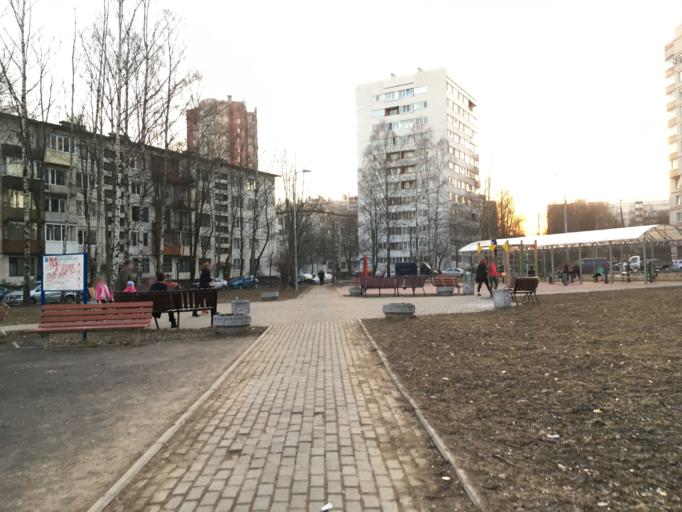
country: RU
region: St.-Petersburg
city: Grazhdanka
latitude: 60.0295
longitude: 30.4108
